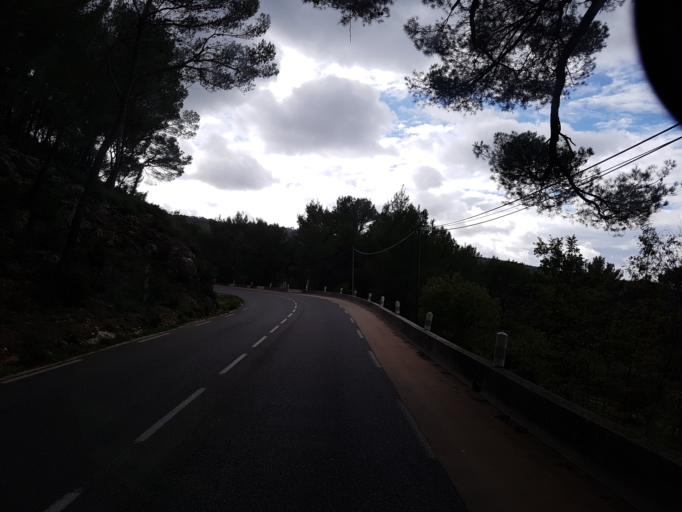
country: FR
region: Provence-Alpes-Cote d'Azur
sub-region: Departement des Bouches-du-Rhone
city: Cuges-les-Pins
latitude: 43.2702
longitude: 5.7180
